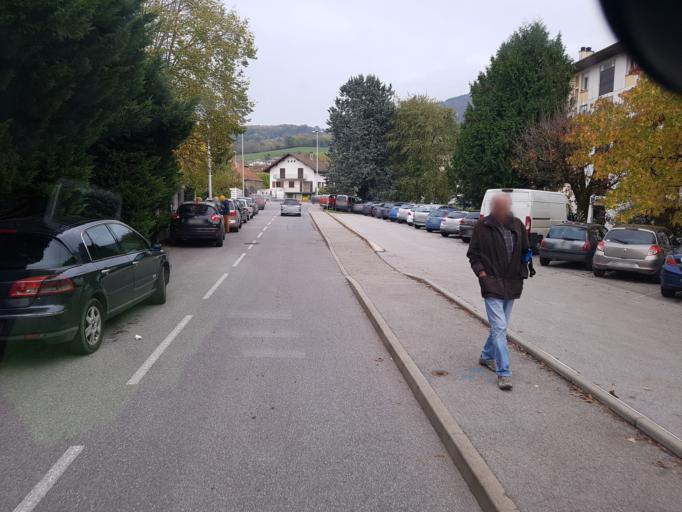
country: FR
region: Rhone-Alpes
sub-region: Departement de la Haute-Savoie
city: Versonnex
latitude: 45.9576
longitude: 5.8372
